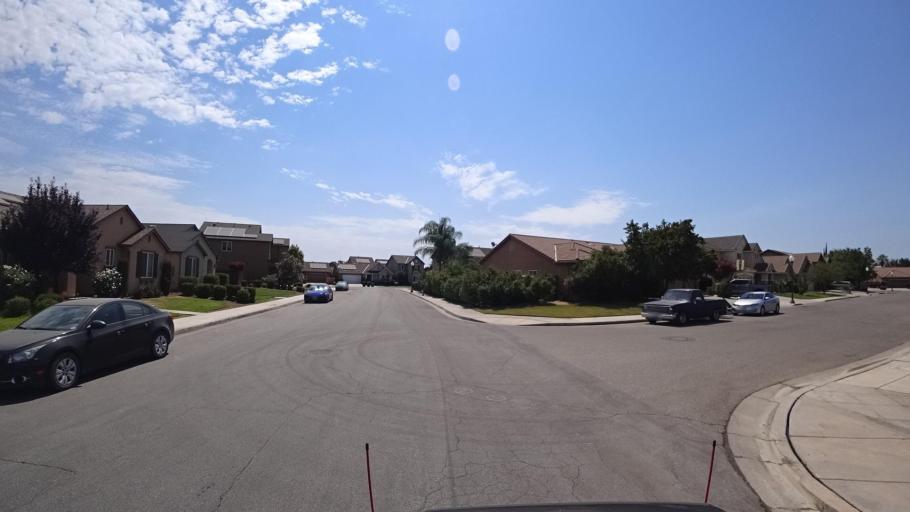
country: US
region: California
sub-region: Fresno County
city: Sunnyside
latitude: 36.7384
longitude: -119.6860
